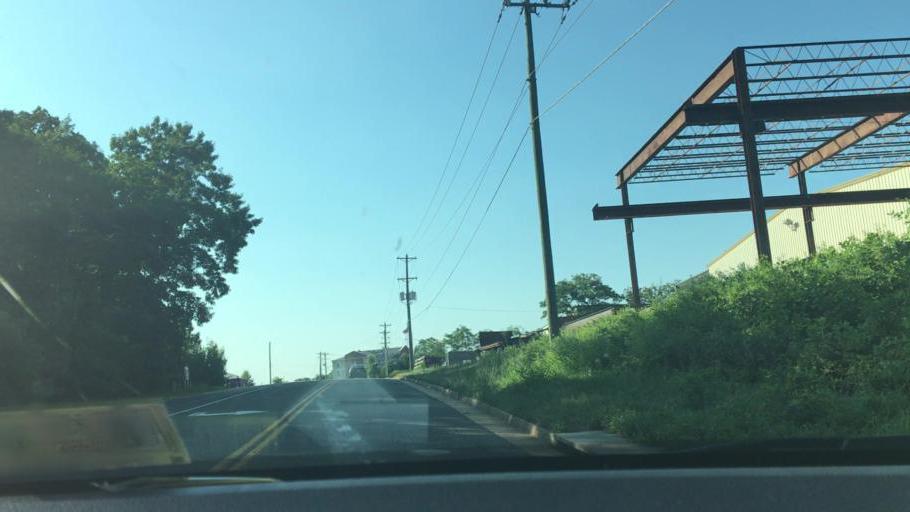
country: US
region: Virginia
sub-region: Prince William County
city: Potomac Mills
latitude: 38.6463
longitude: -77.2885
